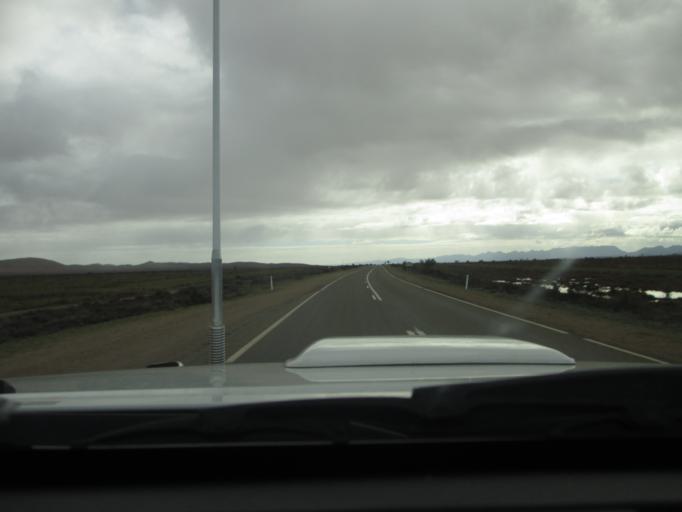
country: AU
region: South Australia
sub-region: Flinders Ranges
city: Quorn
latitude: -31.5440
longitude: 138.4244
